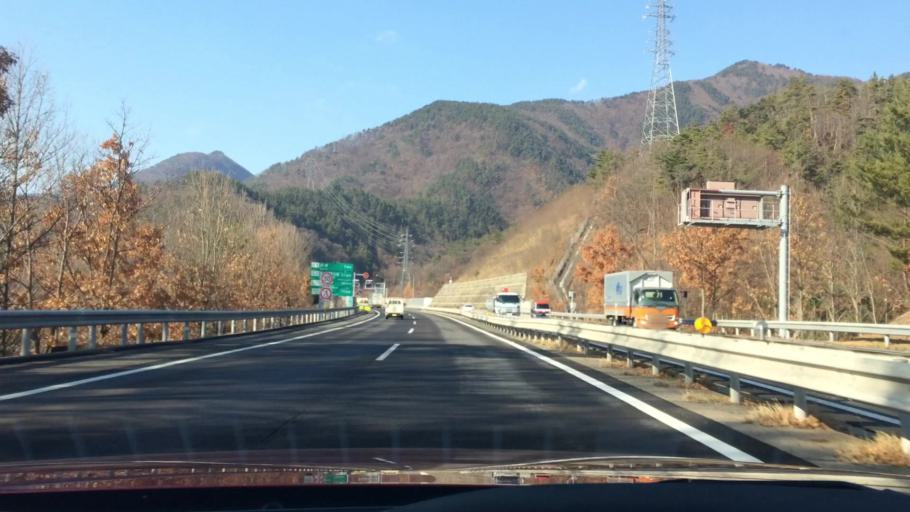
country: JP
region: Nagano
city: Ueda
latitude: 36.4178
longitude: 138.2801
